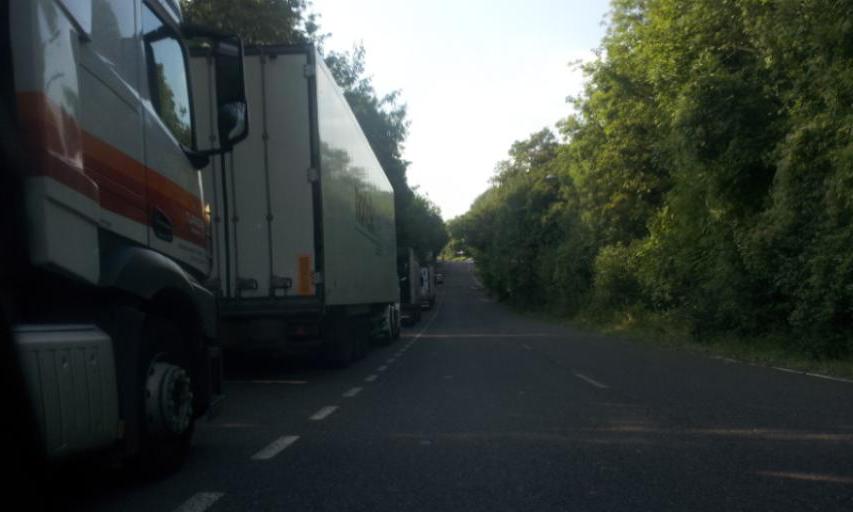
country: GB
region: England
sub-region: Kent
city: Aylesford
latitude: 51.3164
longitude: 0.5093
